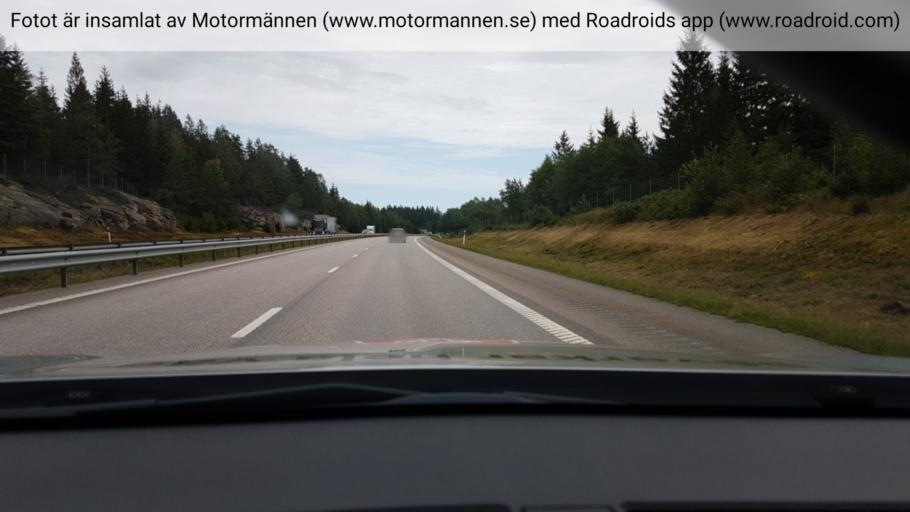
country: SE
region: Vaestra Goetaland
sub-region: Bollebygds Kommun
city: Bollebygd
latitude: 57.6745
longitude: 12.6772
